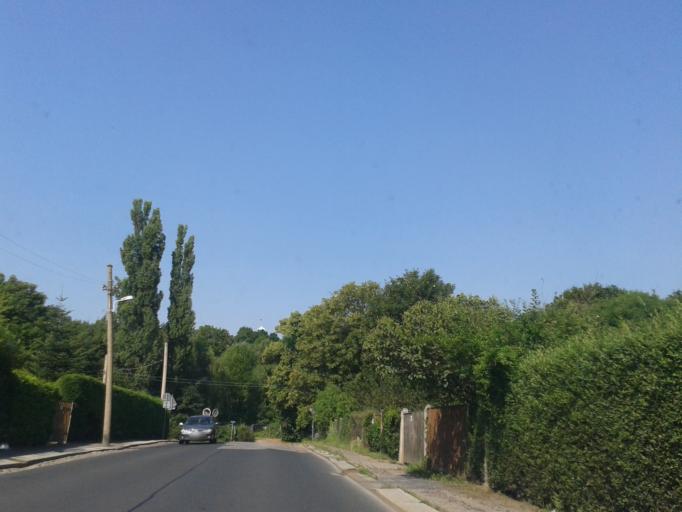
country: DE
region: Saxony
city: Freital
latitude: 51.0357
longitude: 13.6851
